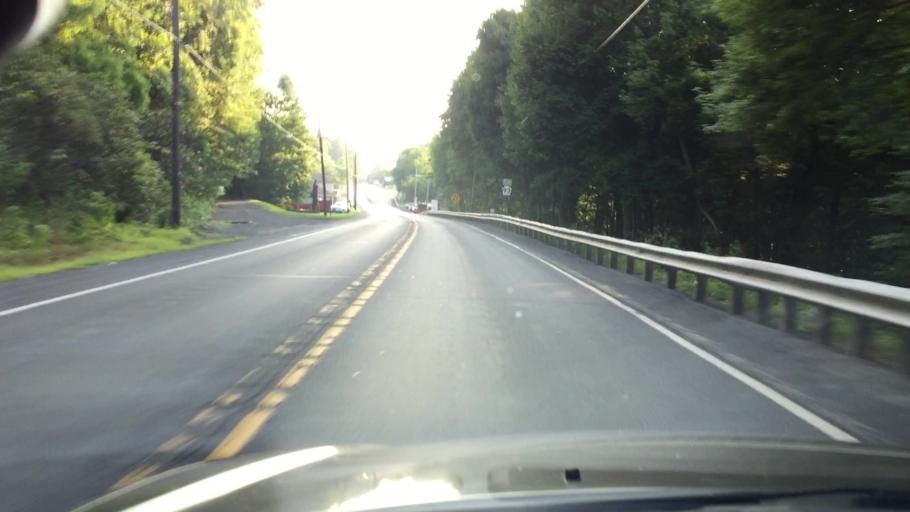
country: US
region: Pennsylvania
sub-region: Carbon County
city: Nesquehoning
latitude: 40.8699
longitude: -75.7842
